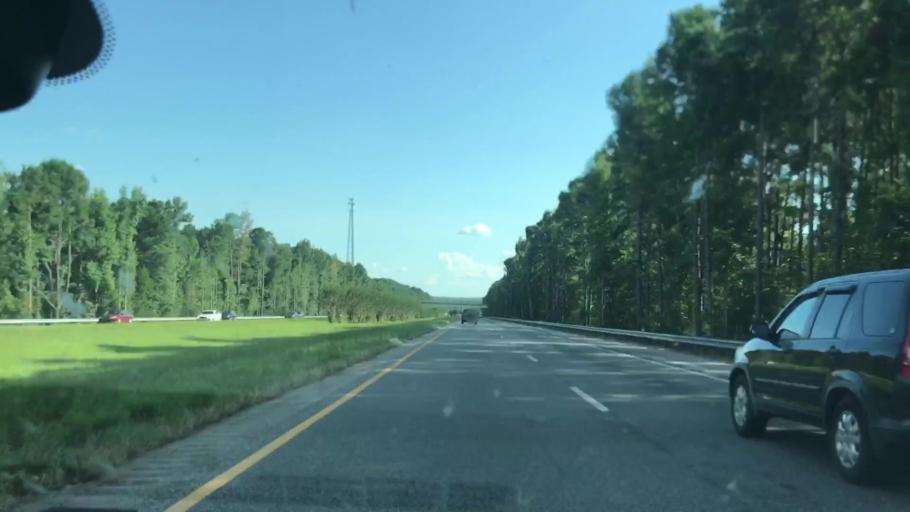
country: US
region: Georgia
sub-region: Harris County
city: Pine Mountain
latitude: 32.9165
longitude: -84.9473
